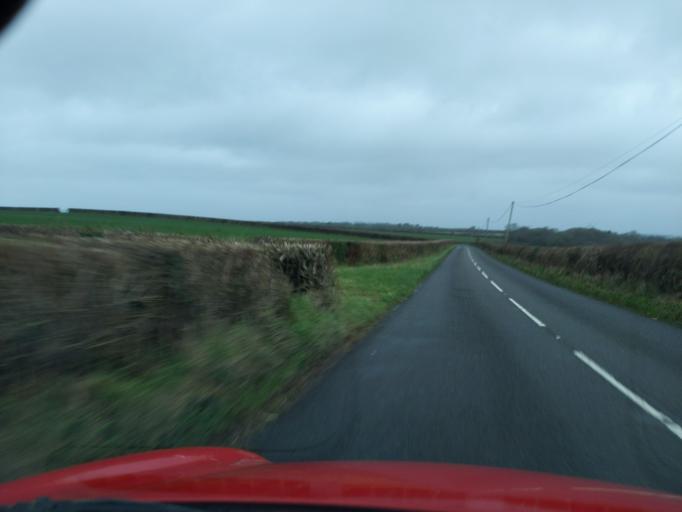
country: GB
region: England
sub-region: Cornwall
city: Boyton
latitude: 50.7256
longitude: -4.3275
